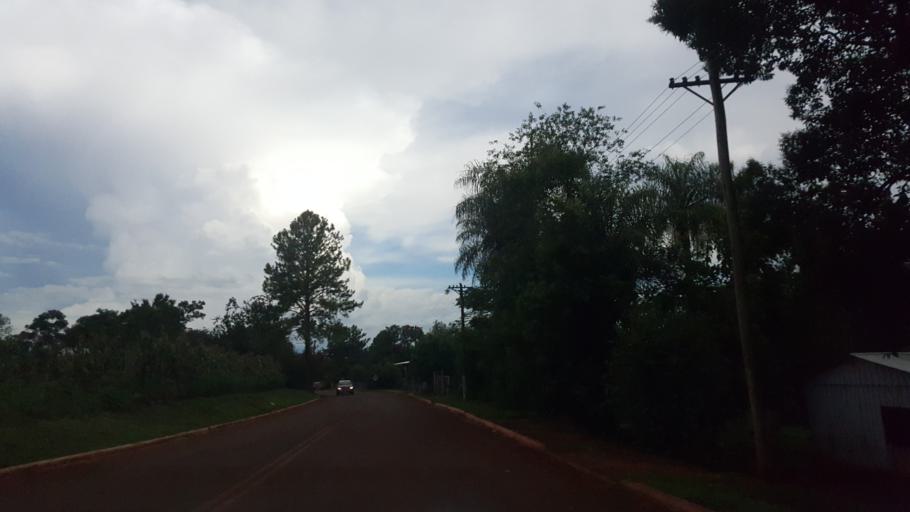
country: AR
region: Misiones
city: Santo Pipo
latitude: -27.1112
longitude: -55.3773
